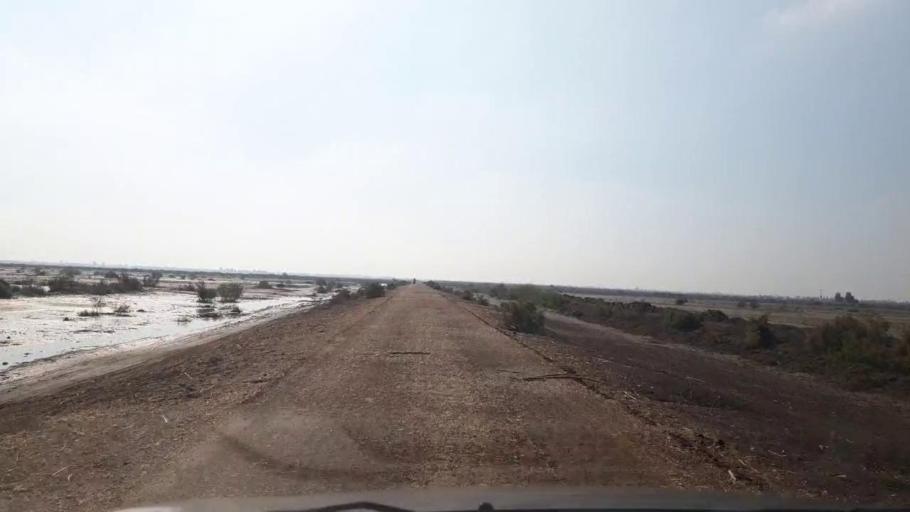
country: PK
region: Sindh
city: Sinjhoro
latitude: 26.0347
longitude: 68.7787
